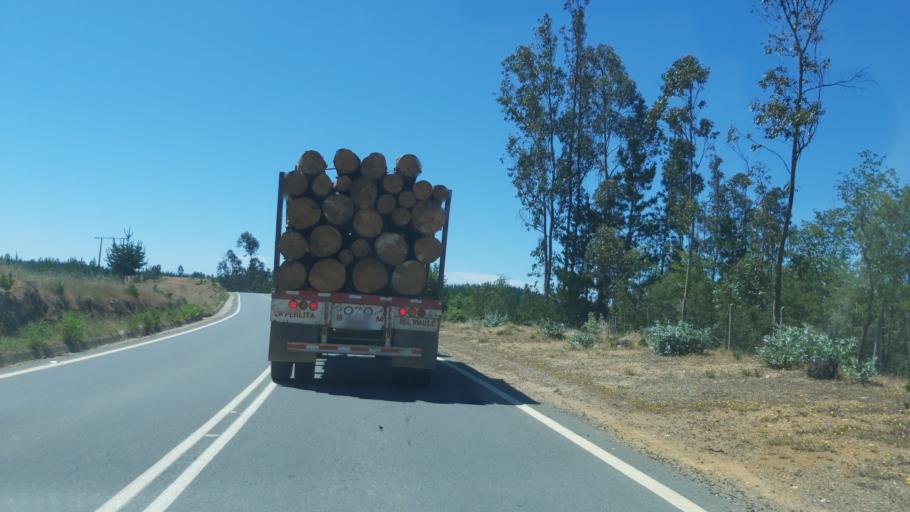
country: CL
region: Maule
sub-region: Provincia de Talca
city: Talca
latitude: -34.9459
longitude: -71.9752
